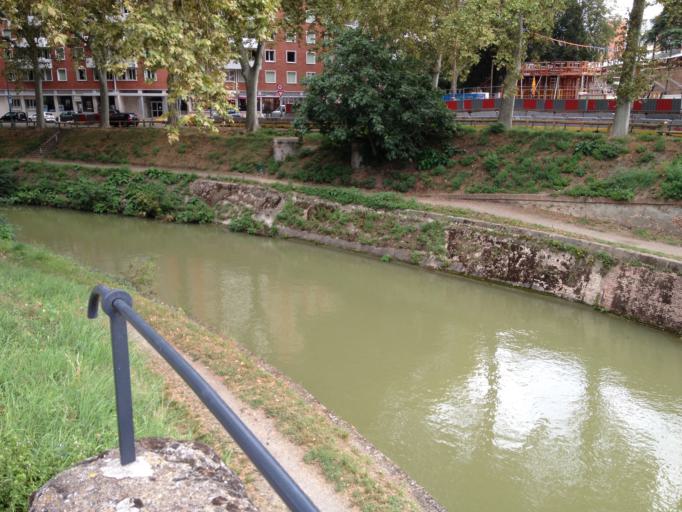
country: FR
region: Midi-Pyrenees
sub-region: Departement de la Haute-Garonne
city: Toulouse
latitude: 43.6047
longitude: 1.4342
